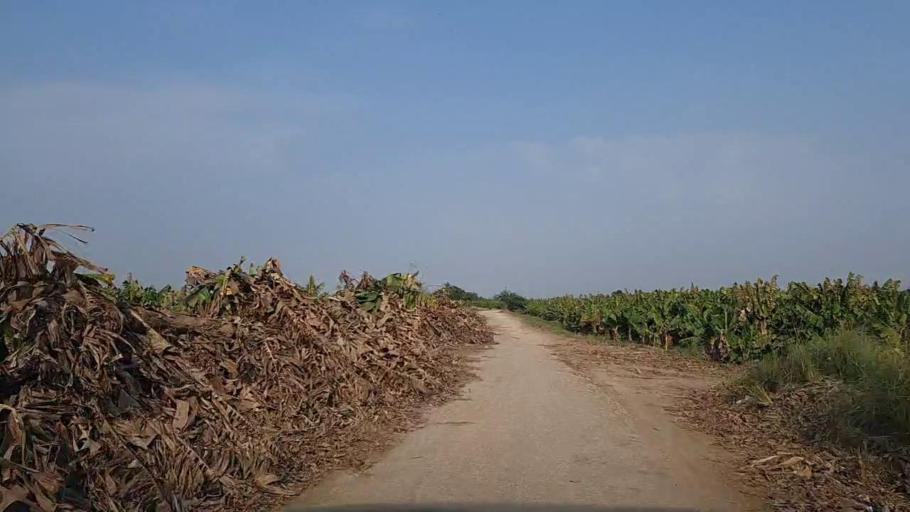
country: PK
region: Sindh
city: Thatta
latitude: 24.6431
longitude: 67.9412
